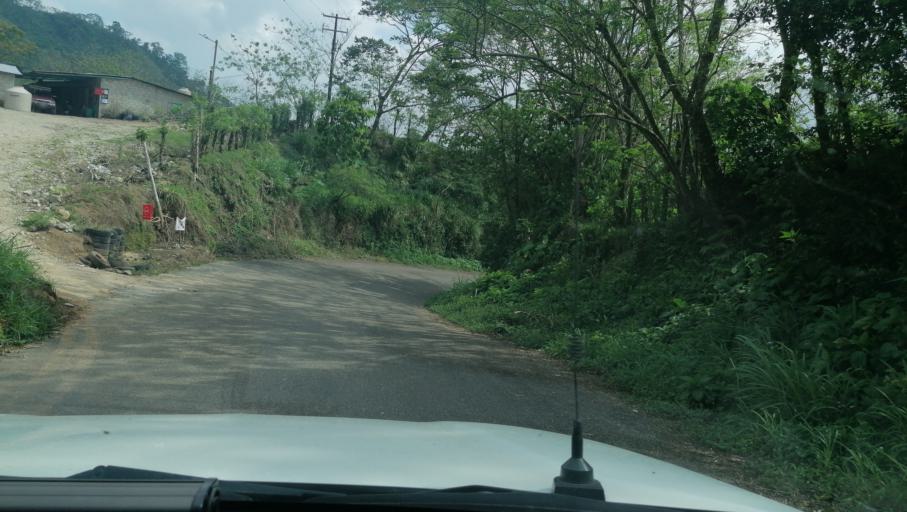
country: MX
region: Chiapas
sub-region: Francisco Leon
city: San Miguel la Sardina
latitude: 17.2387
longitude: -93.3175
